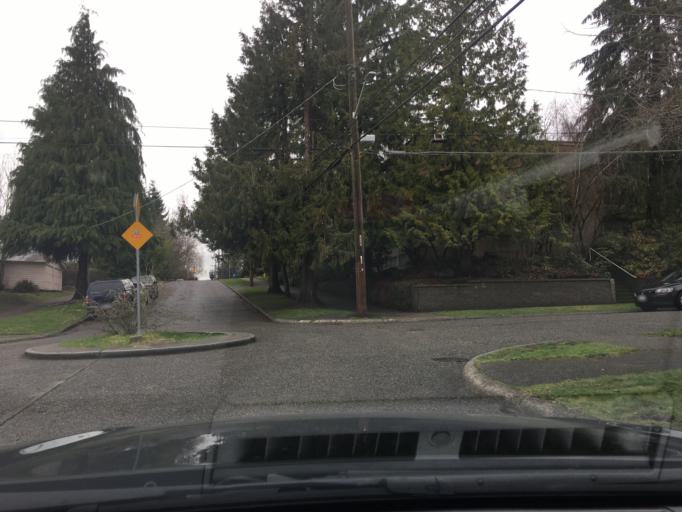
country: US
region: Washington
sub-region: King County
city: Seattle
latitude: 47.6626
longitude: -122.3288
